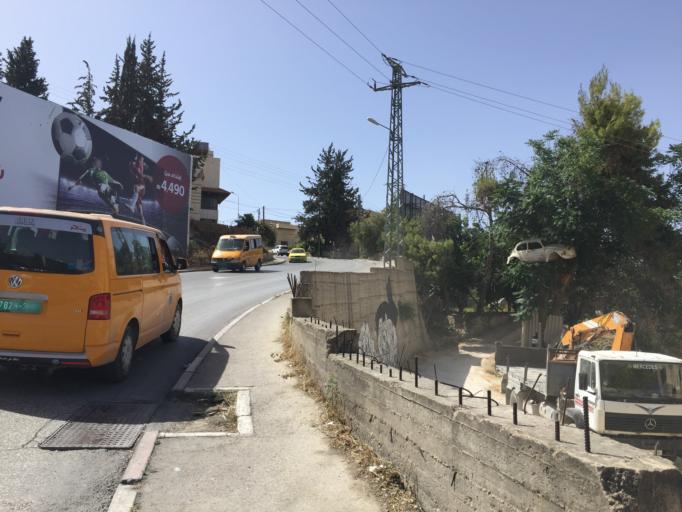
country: PS
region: West Bank
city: Bethlehem
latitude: 31.7047
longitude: 35.2127
